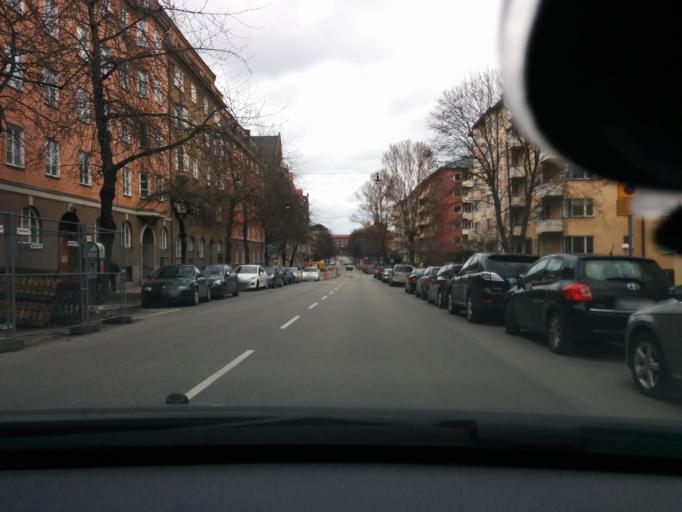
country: SE
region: Stockholm
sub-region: Stockholms Kommun
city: OEstermalm
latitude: 59.3373
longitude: 18.0949
